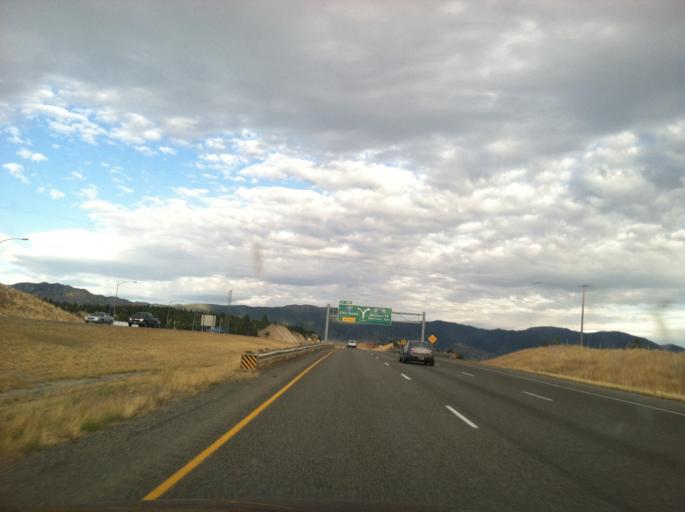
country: US
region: Montana
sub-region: Silver Bow County
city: Butte
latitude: 46.0059
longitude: -112.5947
